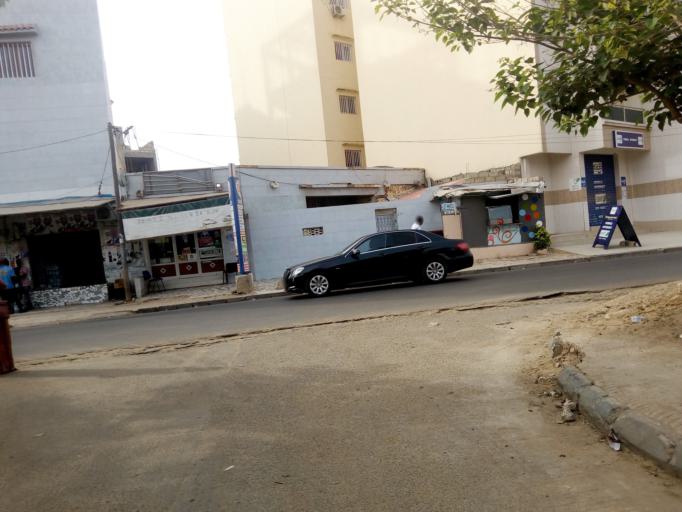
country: SN
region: Dakar
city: Dakar
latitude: 14.6983
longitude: -17.4559
